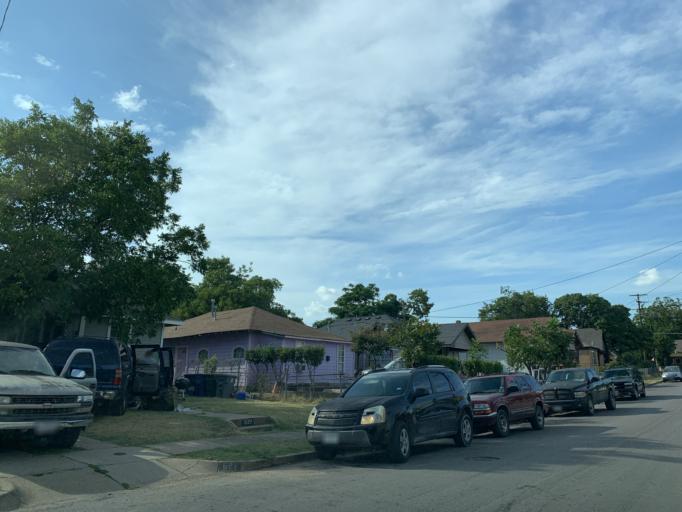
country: US
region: Texas
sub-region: Dallas County
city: Cockrell Hill
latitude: 32.7393
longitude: -96.8361
